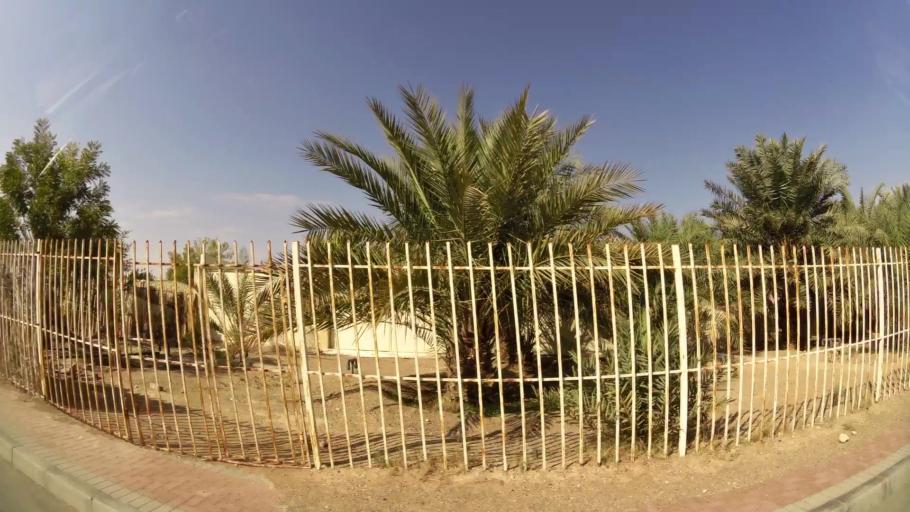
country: AE
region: Abu Dhabi
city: Al Ain
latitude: 24.0901
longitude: 55.9357
